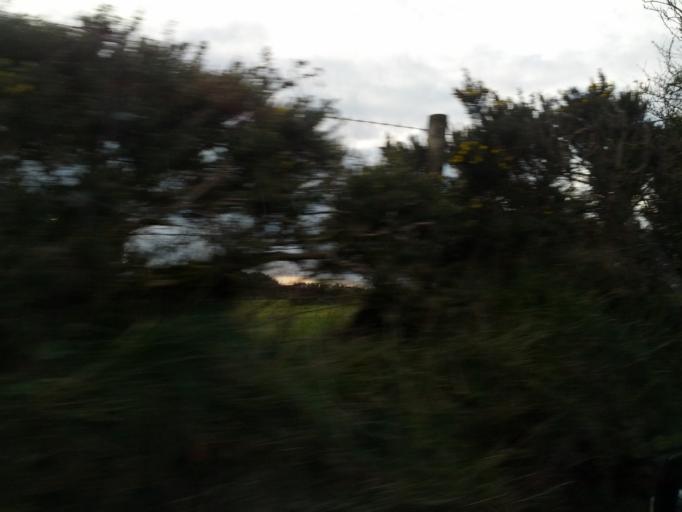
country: IE
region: Connaught
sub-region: County Galway
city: Athenry
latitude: 53.3813
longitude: -8.7179
